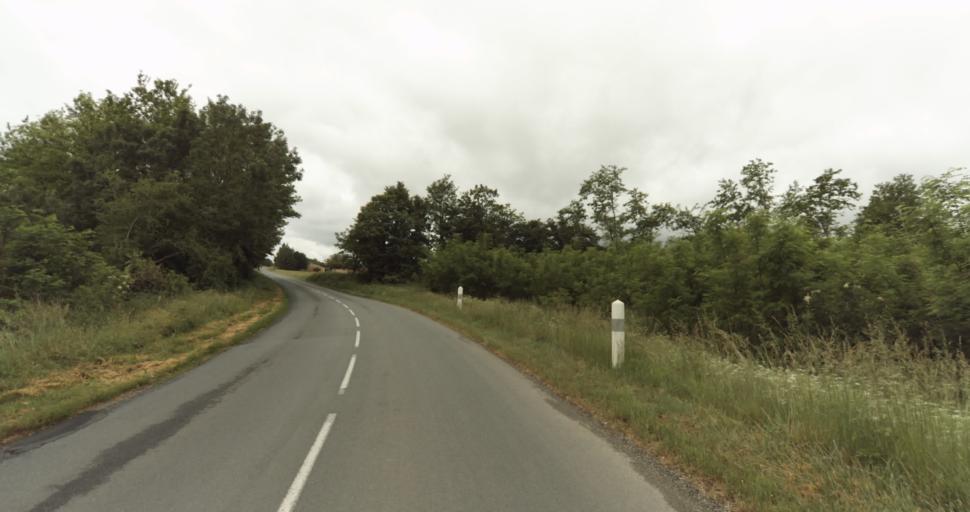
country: FR
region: Aquitaine
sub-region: Departement de la Dordogne
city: Belves
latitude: 44.6921
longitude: 0.9086
